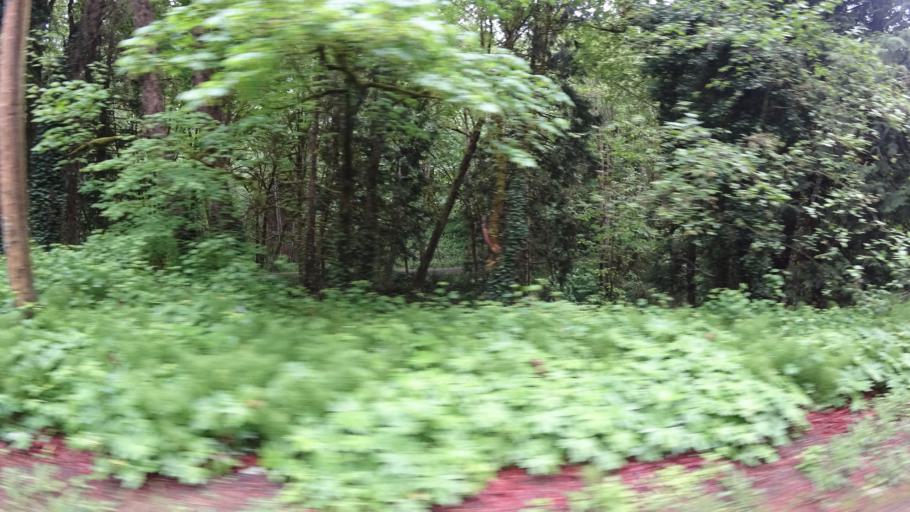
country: US
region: Oregon
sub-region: Washington County
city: West Haven-Sylvan
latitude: 45.5399
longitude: -122.7419
